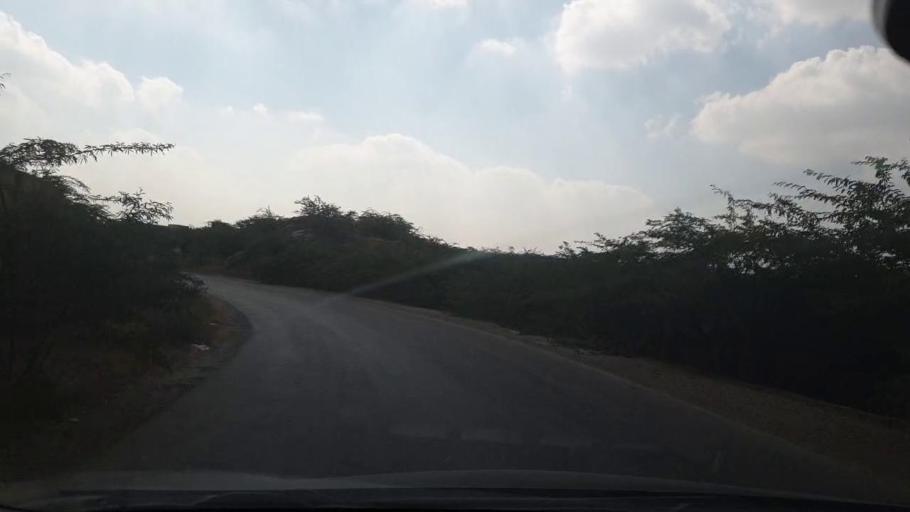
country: PK
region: Sindh
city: Malir Cantonment
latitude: 25.0145
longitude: 67.3525
